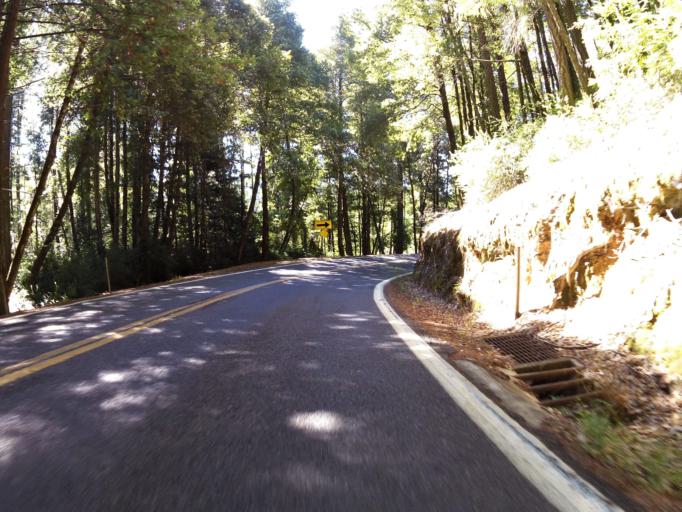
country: US
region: California
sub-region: Humboldt County
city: Redway
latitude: 39.8218
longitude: -123.7808
